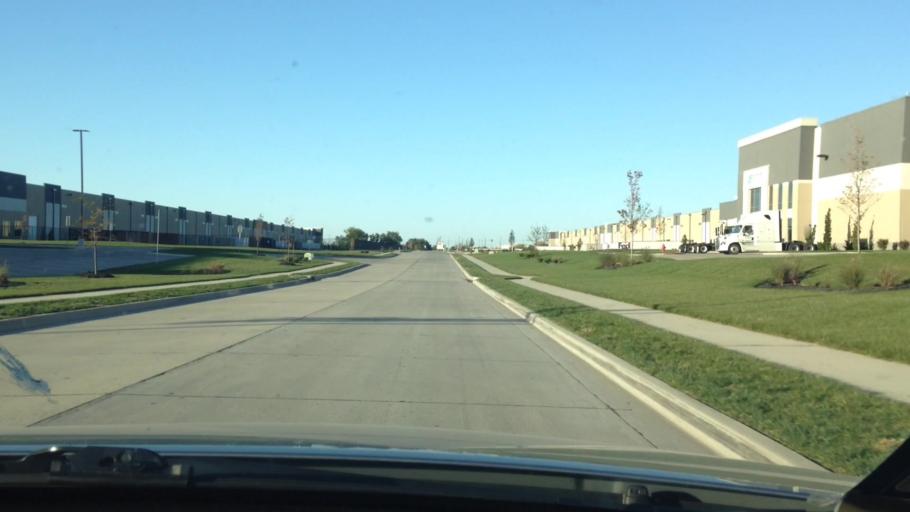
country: US
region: Kansas
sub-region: Johnson County
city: Gardner
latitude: 38.7757
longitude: -94.9423
